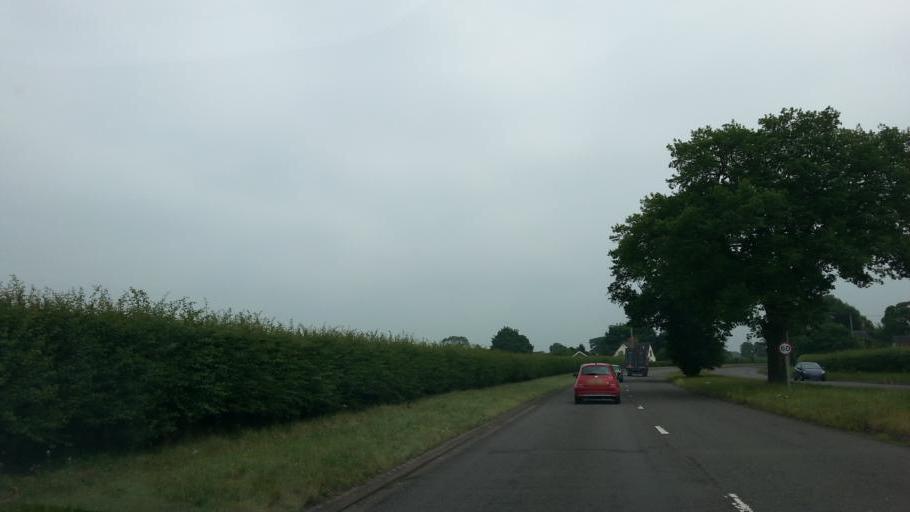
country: GB
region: England
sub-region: Staffordshire
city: Stafford
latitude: 52.8482
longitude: -2.0453
